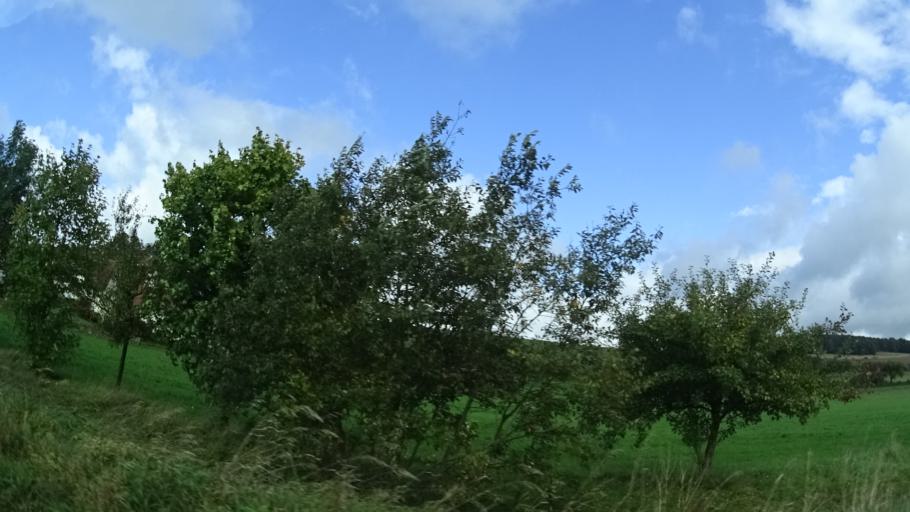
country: DE
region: Bavaria
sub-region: Upper Franconia
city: Burgwindheim
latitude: 49.8791
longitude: 10.6042
